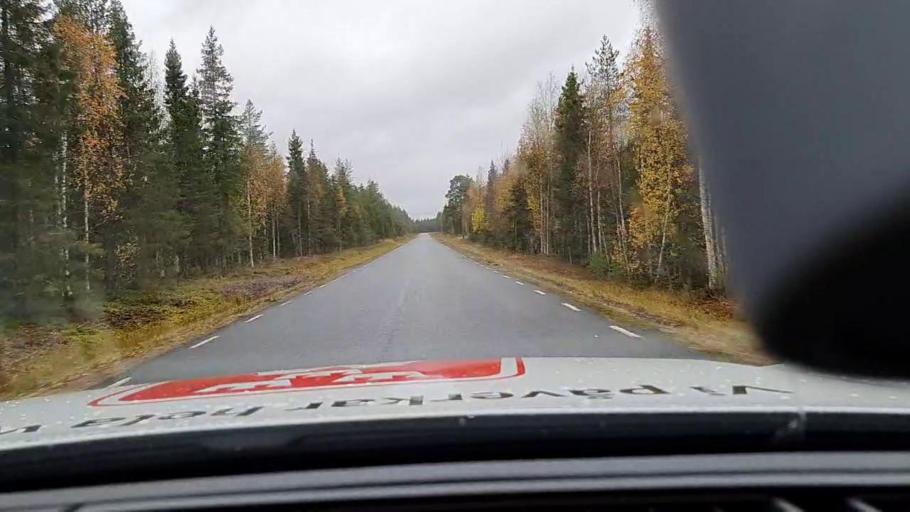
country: SE
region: Norrbotten
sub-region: Haparanda Kommun
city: Haparanda
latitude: 65.9350
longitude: 23.8122
